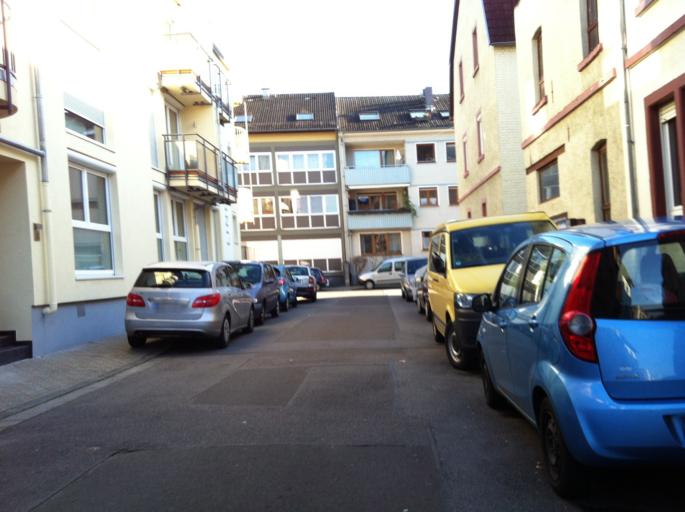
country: DE
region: Baden-Wuerttemberg
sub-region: Karlsruhe Region
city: Heidelberg
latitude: 49.3804
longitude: 8.6833
